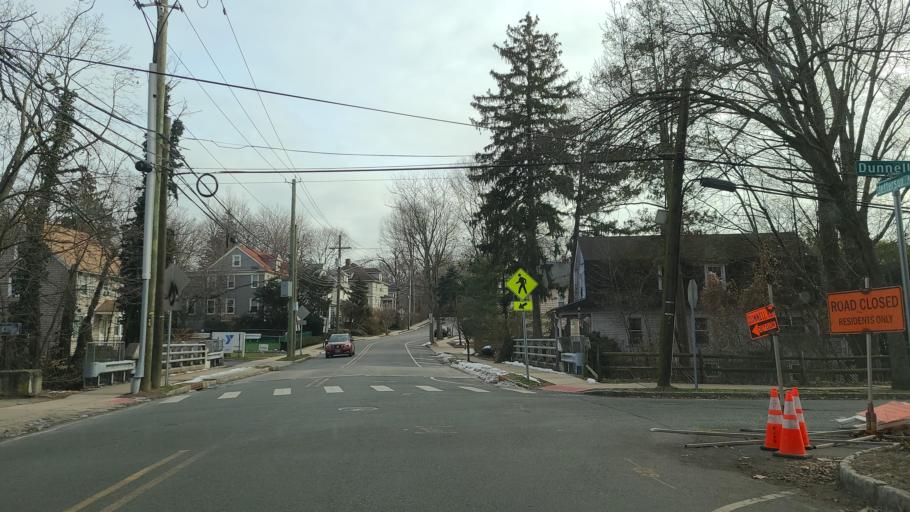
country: US
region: New Jersey
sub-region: Essex County
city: Maplewood
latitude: 40.7350
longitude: -74.2707
